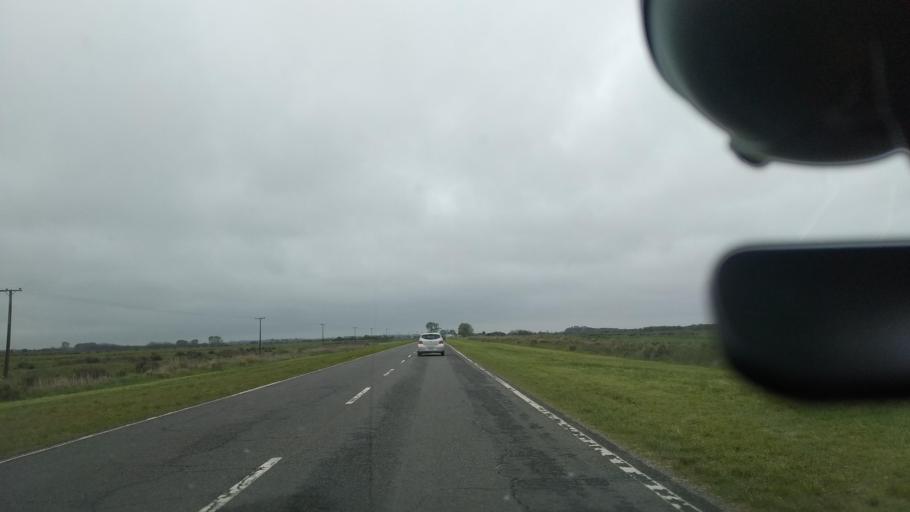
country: AR
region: Buenos Aires
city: Veronica
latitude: -35.6004
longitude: -57.2754
